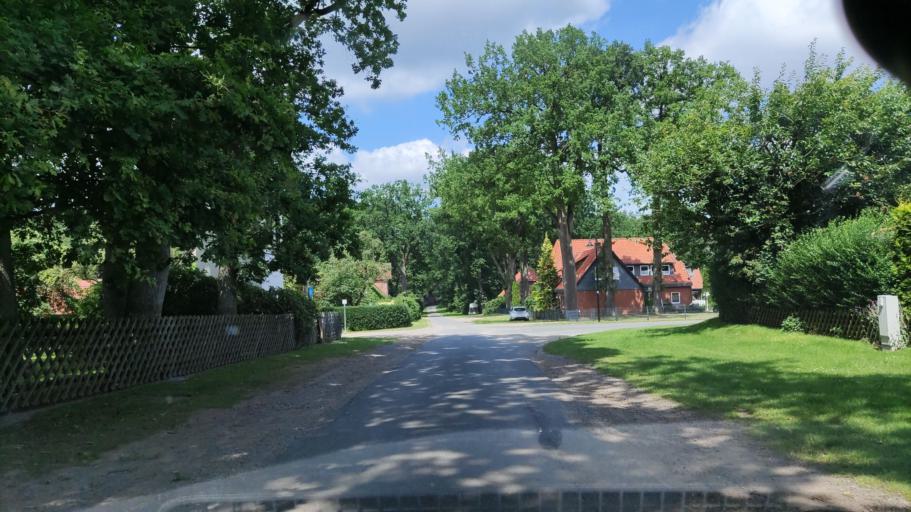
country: DE
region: Lower Saxony
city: Bad Fallingbostel
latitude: 52.8286
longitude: 9.6713
